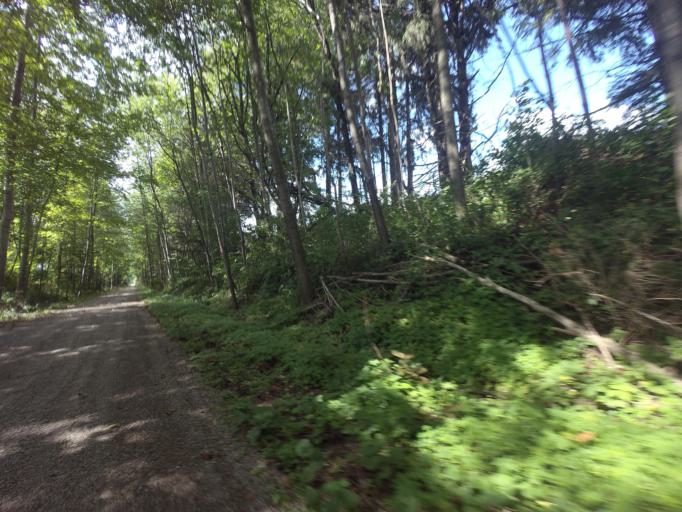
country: CA
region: Ontario
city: Huron East
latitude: 43.7191
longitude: -81.3942
